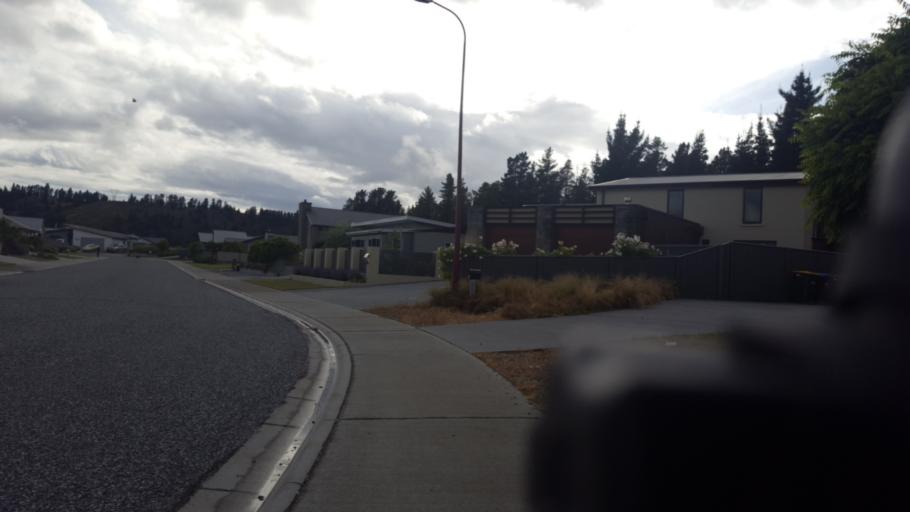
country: NZ
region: Otago
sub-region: Queenstown-Lakes District
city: Wanaka
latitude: -45.2409
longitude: 169.3807
